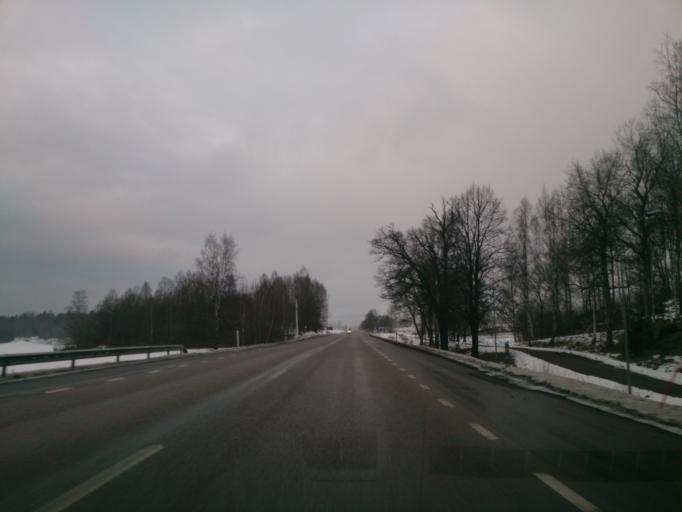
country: SE
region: OEstergoetland
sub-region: Atvidabergs Kommun
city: Atvidaberg
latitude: 58.2170
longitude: 15.9751
